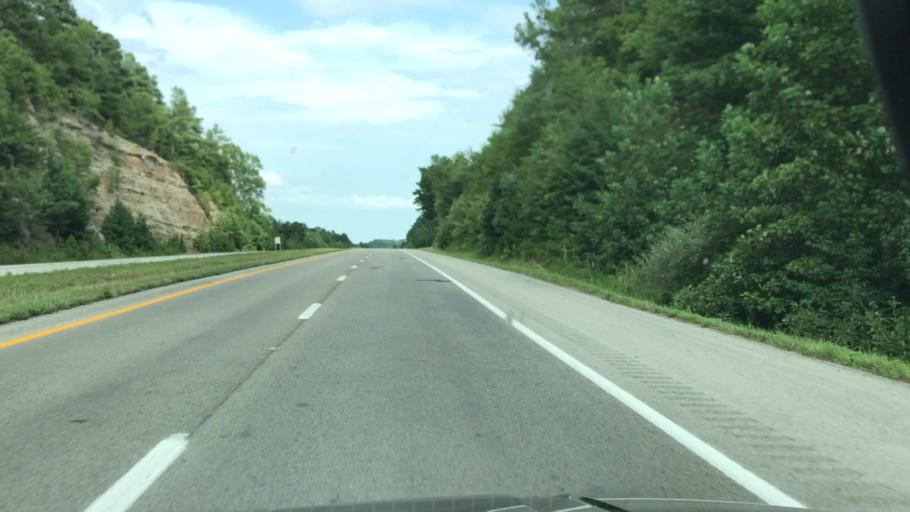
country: US
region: Kentucky
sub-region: Hopkins County
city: Earlington
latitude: 37.2010
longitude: -87.5347
